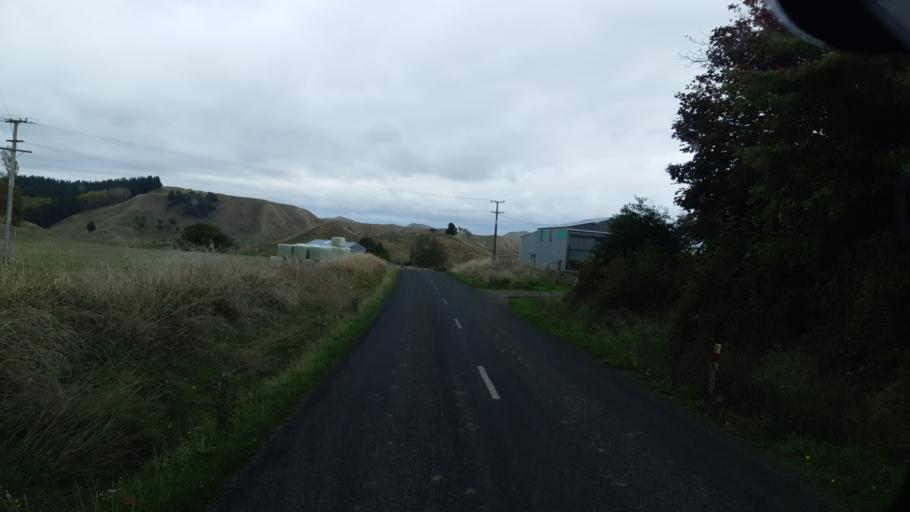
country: NZ
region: Manawatu-Wanganui
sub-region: Ruapehu District
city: Waiouru
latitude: -39.5528
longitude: 175.6073
